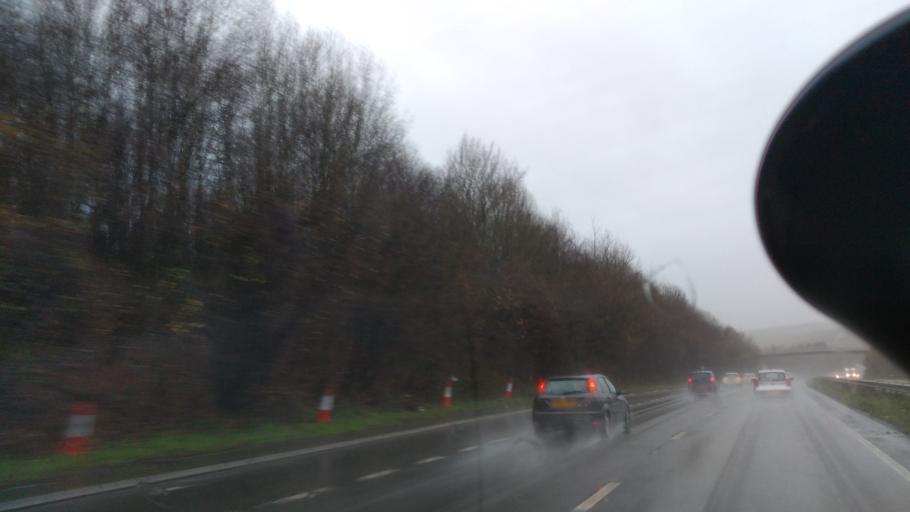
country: GB
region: England
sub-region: Brighton and Hove
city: Brighton
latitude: 50.8692
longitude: -0.1400
